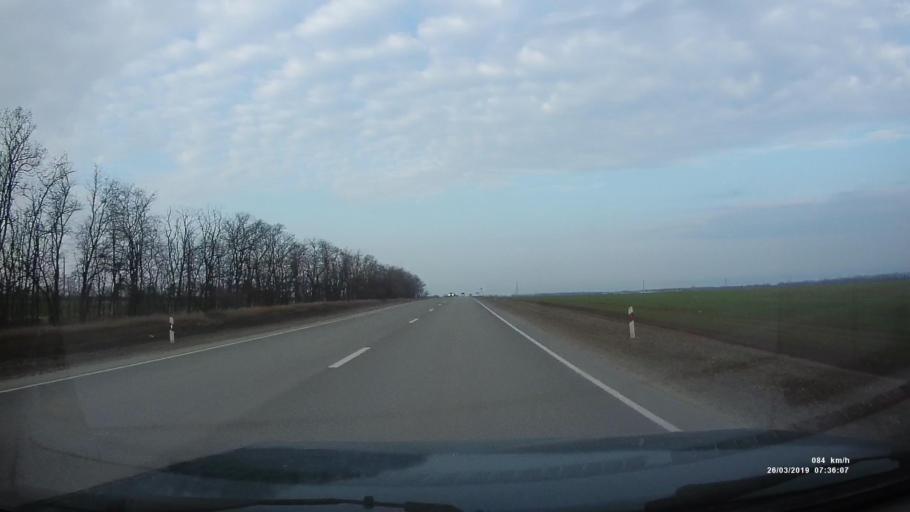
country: RU
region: Rostov
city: Novobessergenovka
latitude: 47.2058
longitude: 38.7261
